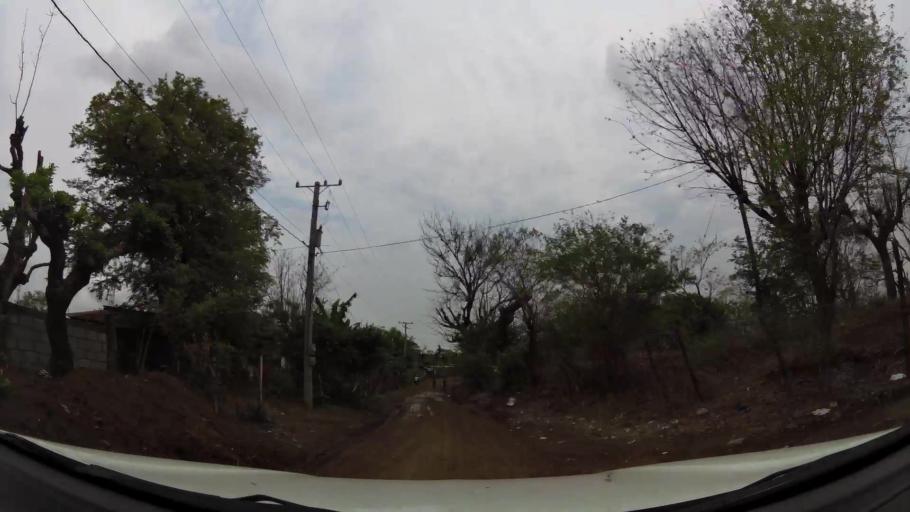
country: NI
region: Granada
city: Granada
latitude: 11.9121
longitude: -85.9654
